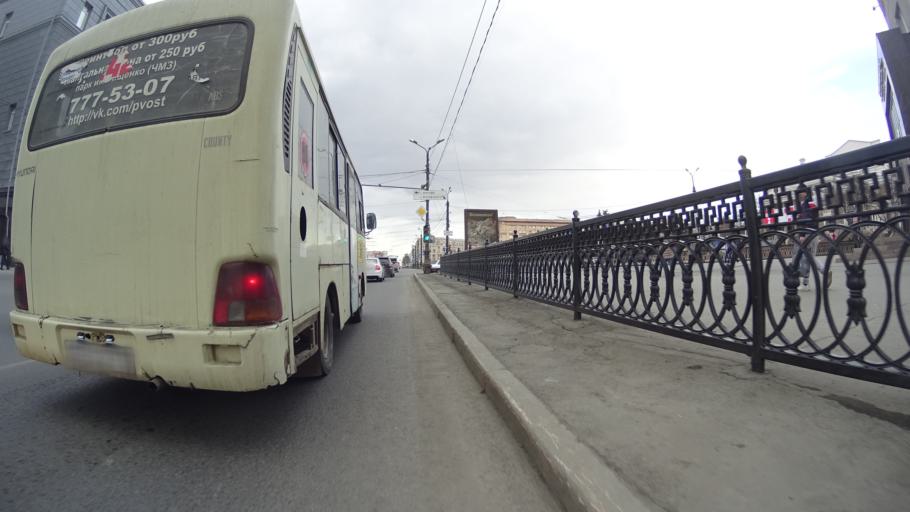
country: RU
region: Chelyabinsk
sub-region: Gorod Chelyabinsk
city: Chelyabinsk
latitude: 55.1601
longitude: 61.3995
